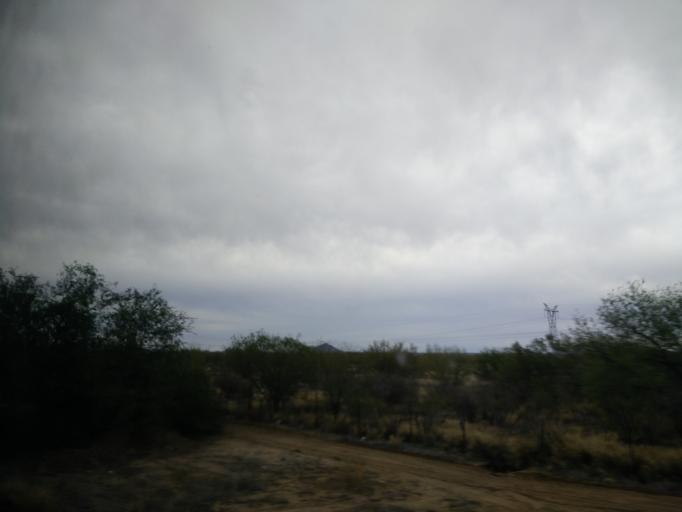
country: MX
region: Sonora
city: Hermosillo
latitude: 28.6891
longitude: -110.9901
